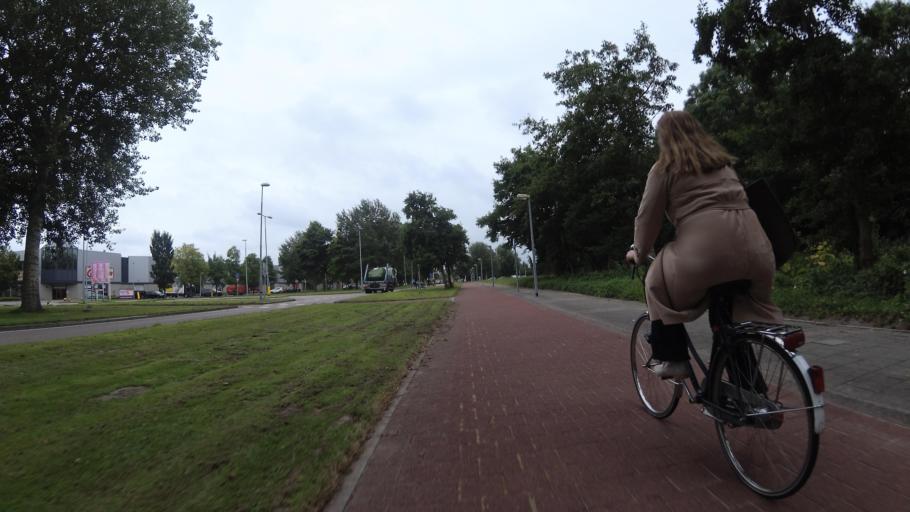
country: NL
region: North Holland
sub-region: Gemeente Den Helder
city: Den Helder
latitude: 52.9438
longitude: 4.7683
